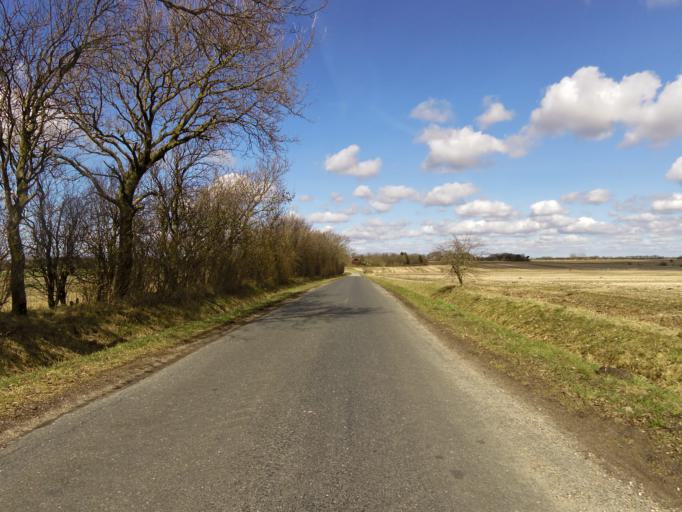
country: DK
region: South Denmark
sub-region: Tonder Kommune
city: Toftlund
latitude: 55.1715
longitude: 9.0872
